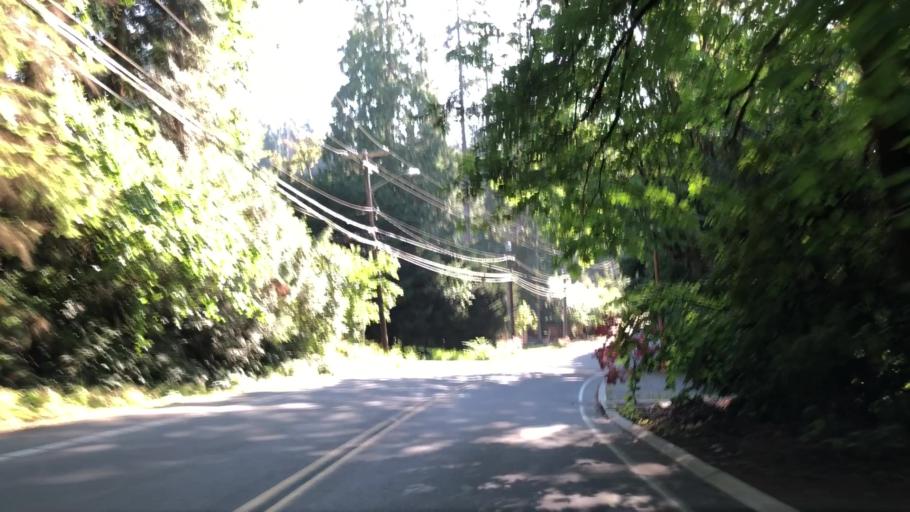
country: US
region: Washington
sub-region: King County
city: Woodinville
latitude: 47.7581
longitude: -122.1204
